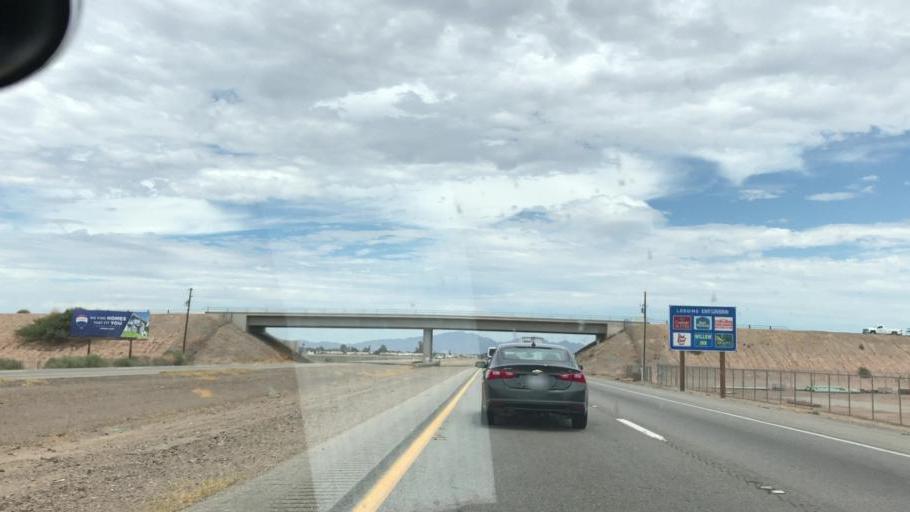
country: US
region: California
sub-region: Riverside County
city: Blythe
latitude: 33.6065
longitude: -114.6419
